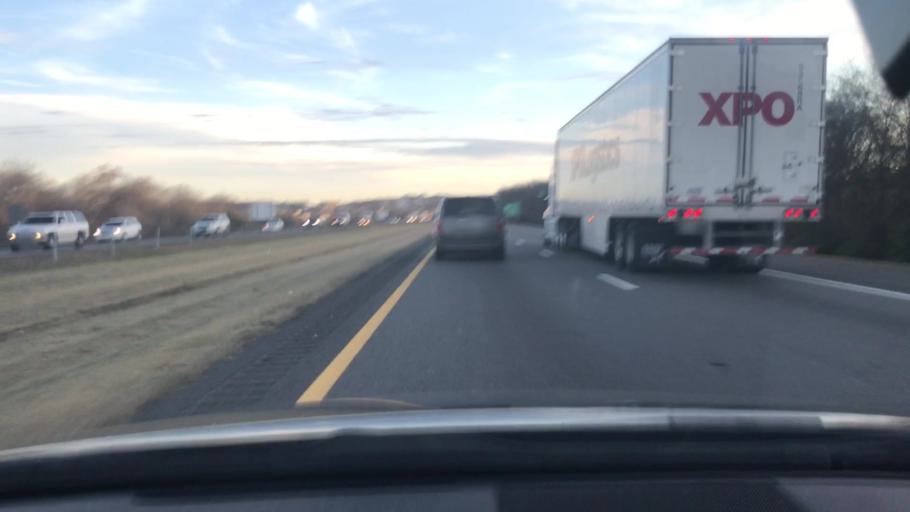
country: US
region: Tennessee
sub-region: Davidson County
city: Goodlettsville
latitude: 36.3323
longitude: -86.7094
